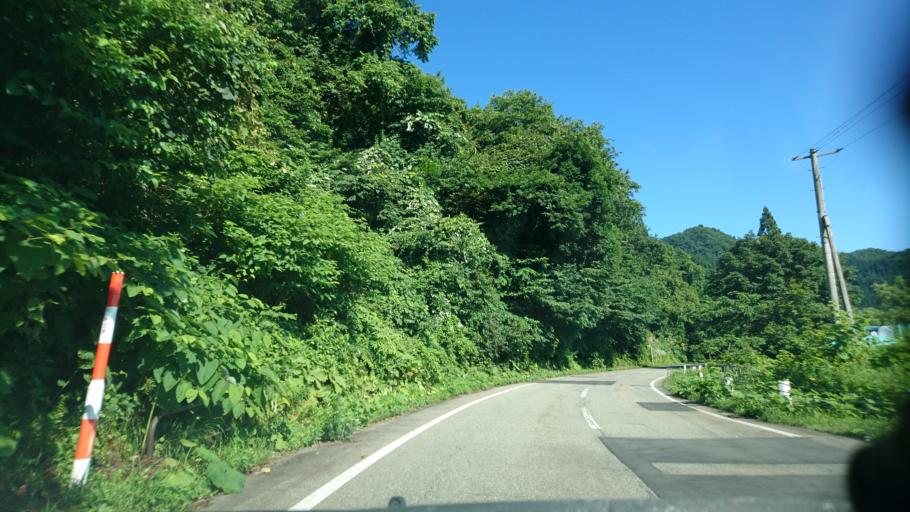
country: JP
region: Akita
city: Kakunodatemachi
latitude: 39.7165
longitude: 140.6307
